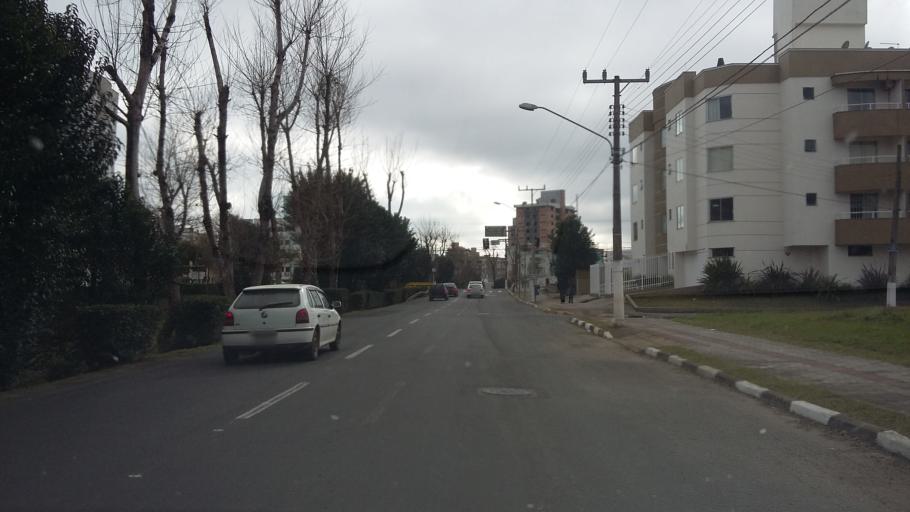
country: BR
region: Santa Catarina
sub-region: Lages
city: Lages
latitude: -27.8210
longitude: -50.3216
